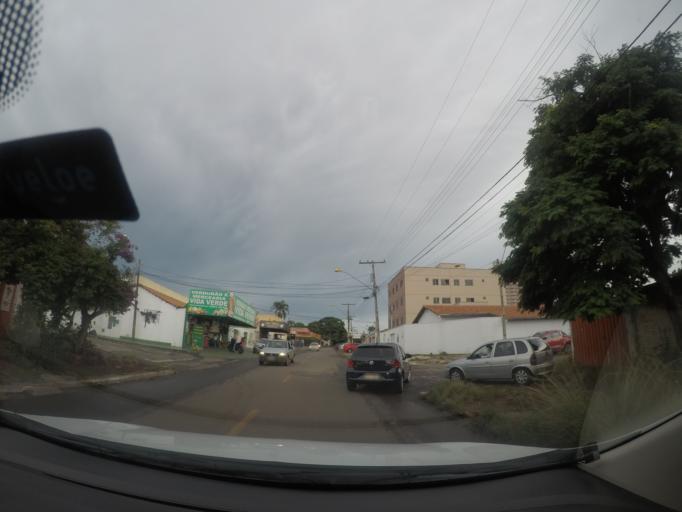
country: BR
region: Goias
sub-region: Goiania
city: Goiania
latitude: -16.6929
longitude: -49.3081
